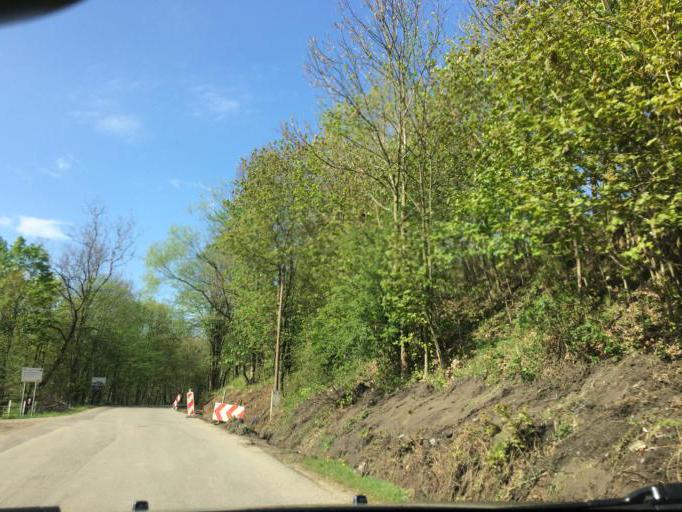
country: PL
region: Lower Silesian Voivodeship
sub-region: Powiat dzierzoniowski
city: Pieszyce
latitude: 50.6895
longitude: 16.5520
